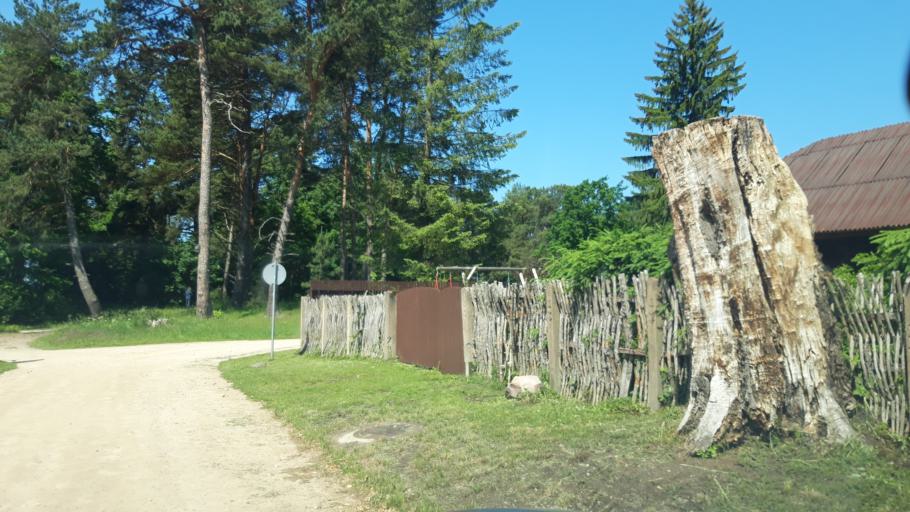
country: LV
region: Saulkrastu
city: Saulkrasti
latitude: 57.2589
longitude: 24.4113
